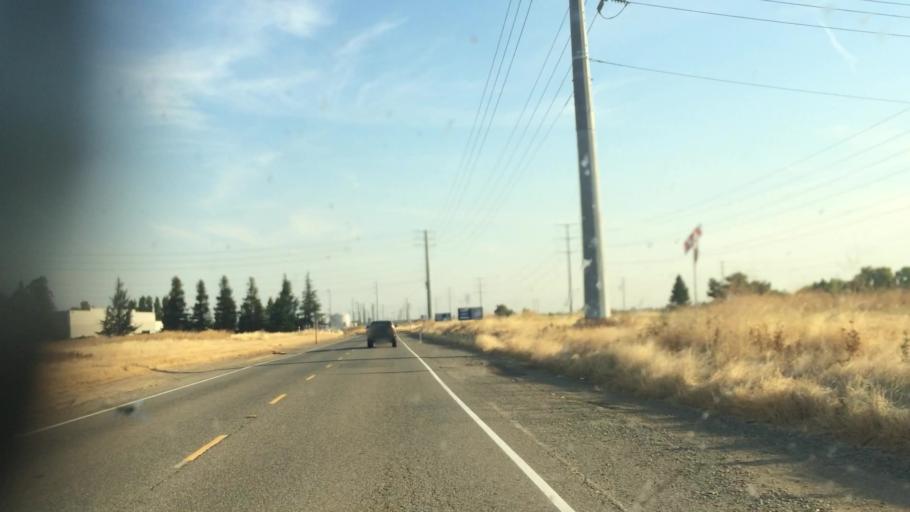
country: US
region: California
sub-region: Sacramento County
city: Laguna
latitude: 38.4432
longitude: -121.4592
